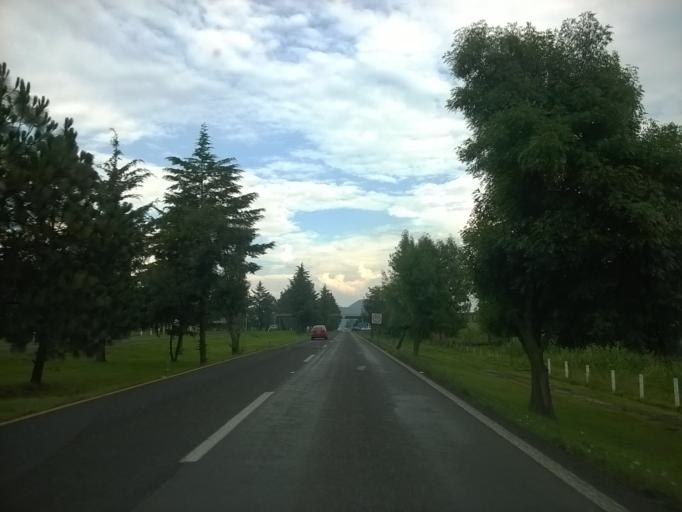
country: MX
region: Michoacan
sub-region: Huiramba
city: El Pedregal
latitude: 19.5310
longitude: -101.4857
